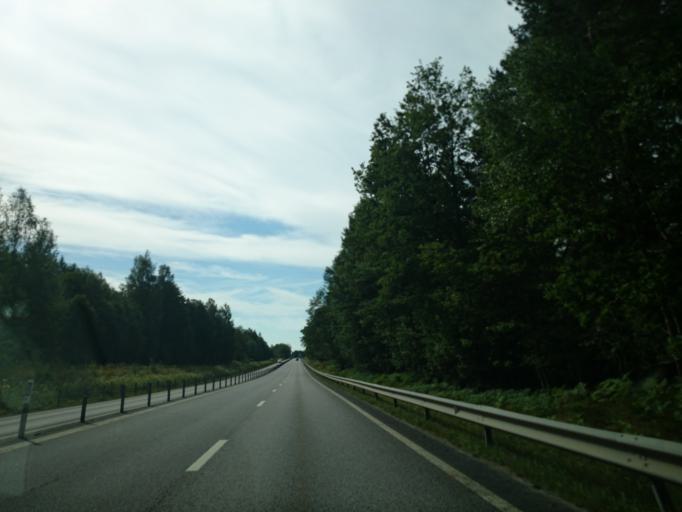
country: SE
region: Kalmar
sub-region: Vasterviks Kommun
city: Vaestervik
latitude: 57.7885
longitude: 16.5259
